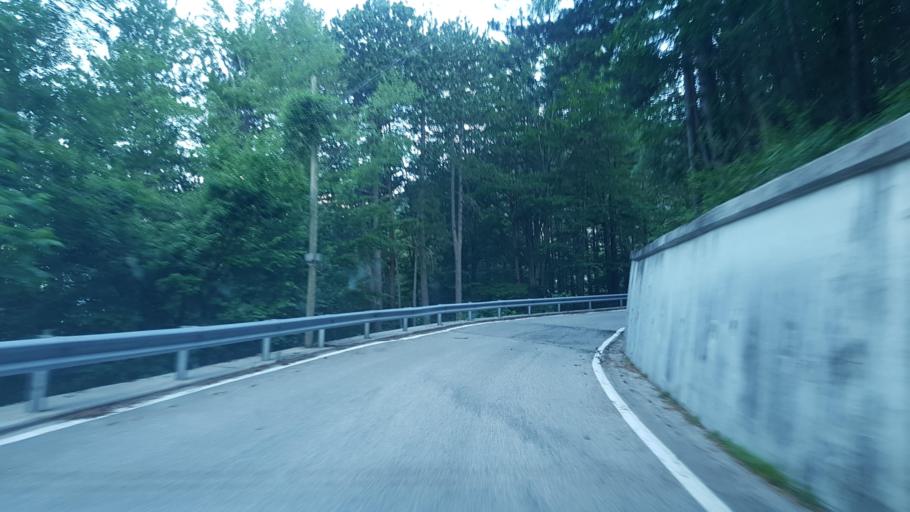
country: IT
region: Friuli Venezia Giulia
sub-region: Provincia di Udine
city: Dogna
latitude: 46.4515
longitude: 13.3581
